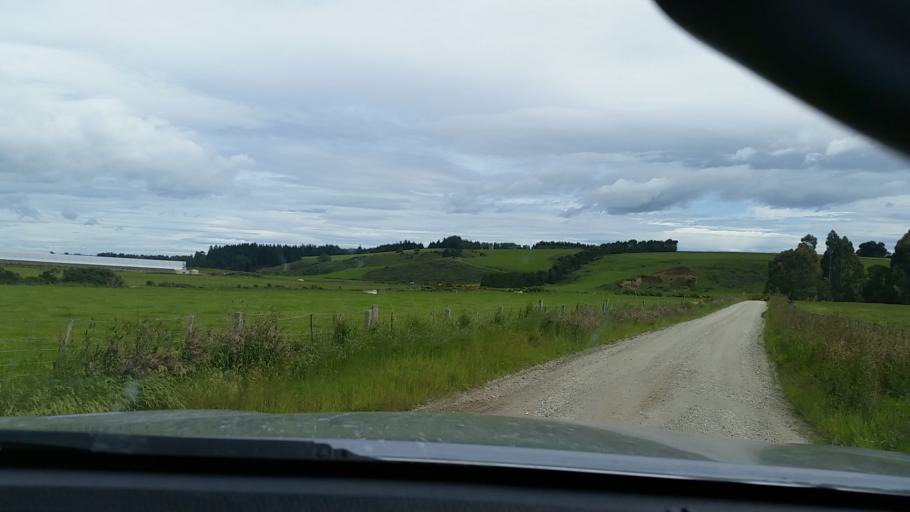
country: NZ
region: Southland
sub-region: Gore District
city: Gore
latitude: -46.2624
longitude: 168.8890
